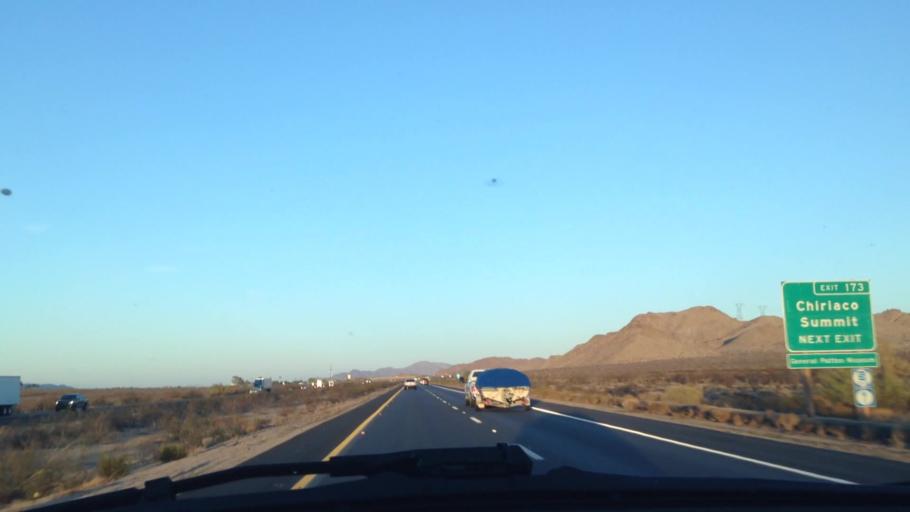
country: US
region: California
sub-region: Riverside County
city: Mecca
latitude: 33.6591
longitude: -115.7379
